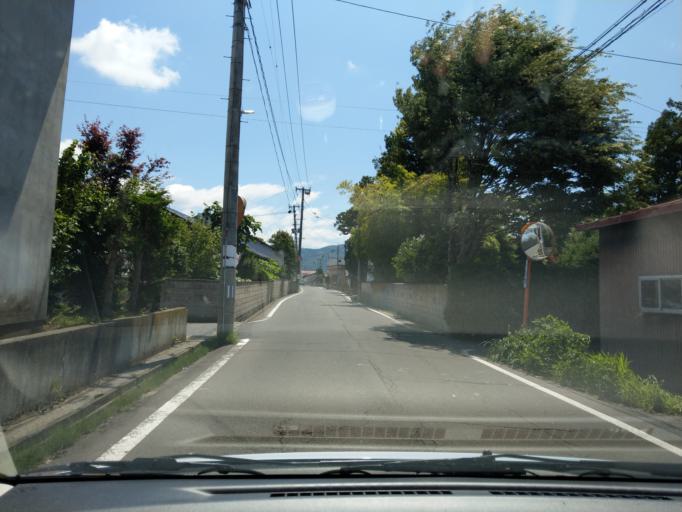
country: JP
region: Aomori
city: Kuroishi
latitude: 40.5750
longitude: 140.5517
